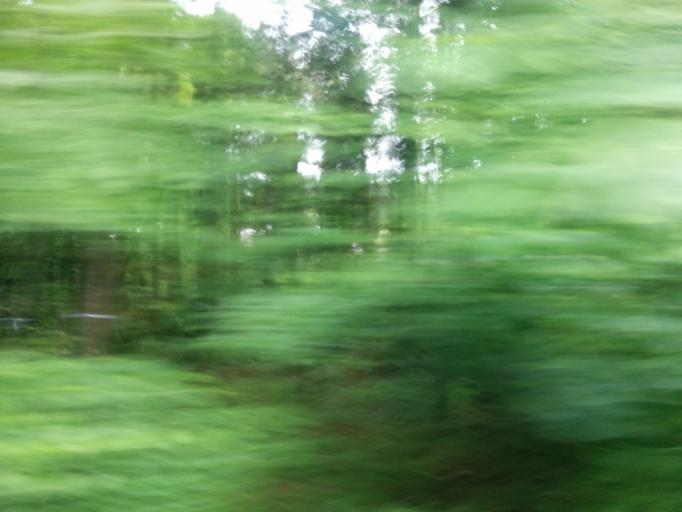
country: JP
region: Tochigi
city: Kanuma
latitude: 36.6009
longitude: 139.7466
